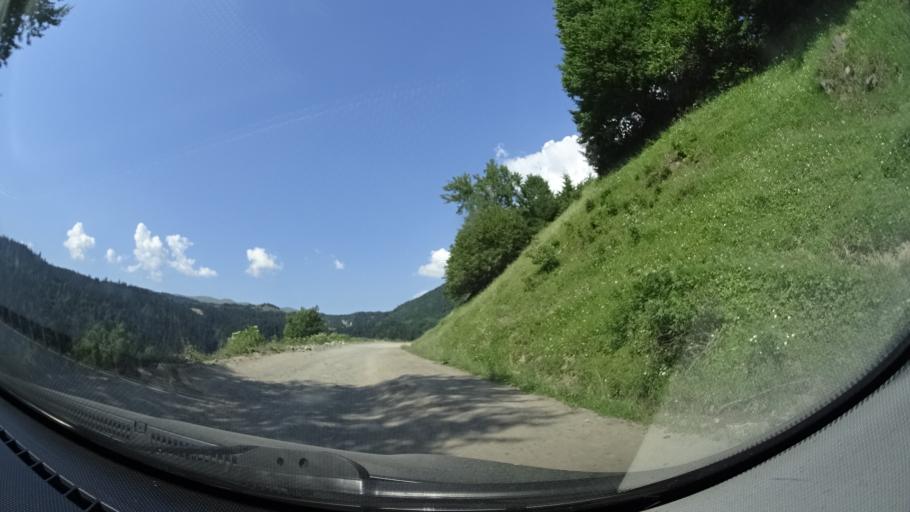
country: GE
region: Ajaria
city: Dioknisi
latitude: 41.6516
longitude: 42.4608
